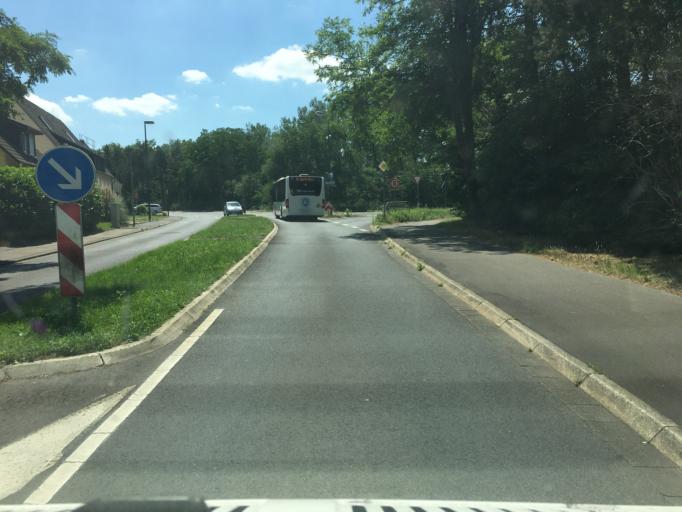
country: DE
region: North Rhine-Westphalia
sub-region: Regierungsbezirk Koln
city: Frechen
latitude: 50.8672
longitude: 6.8150
